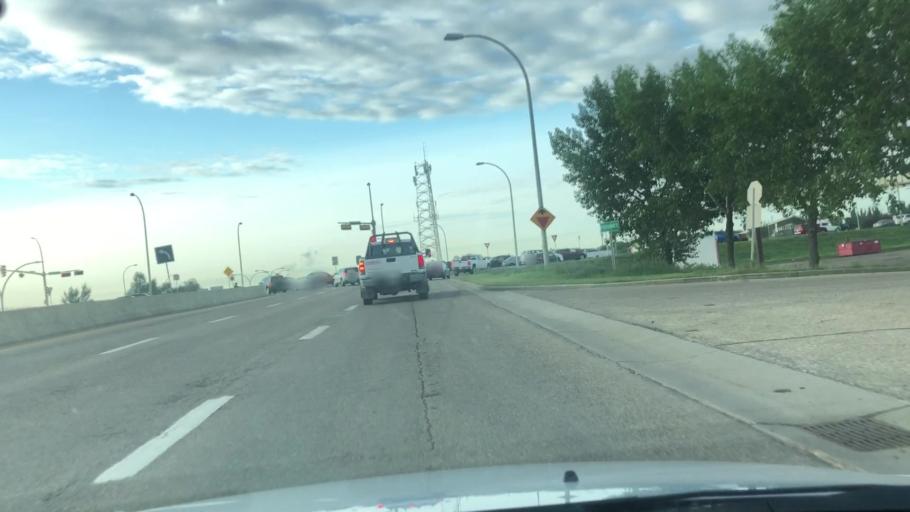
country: CA
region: Alberta
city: Edmonton
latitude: 53.5812
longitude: -113.4542
